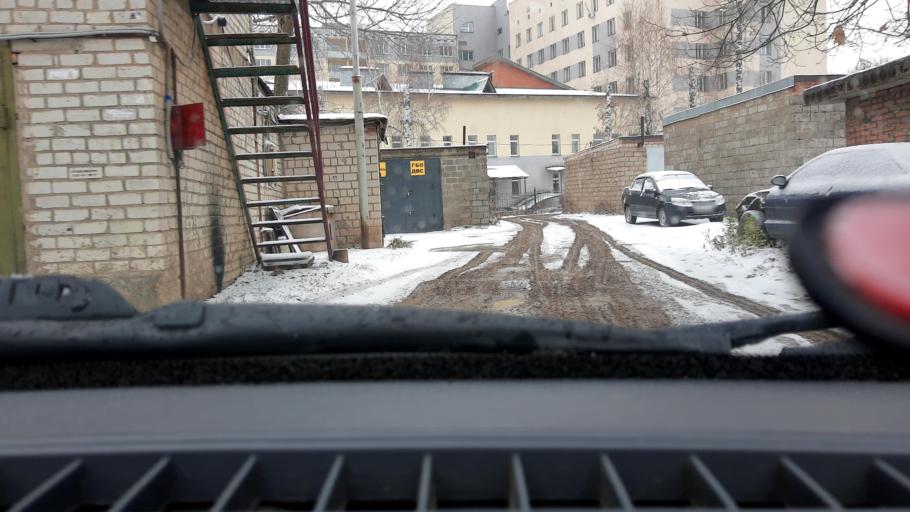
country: RU
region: Bashkortostan
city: Ufa
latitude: 54.8022
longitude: 56.0398
